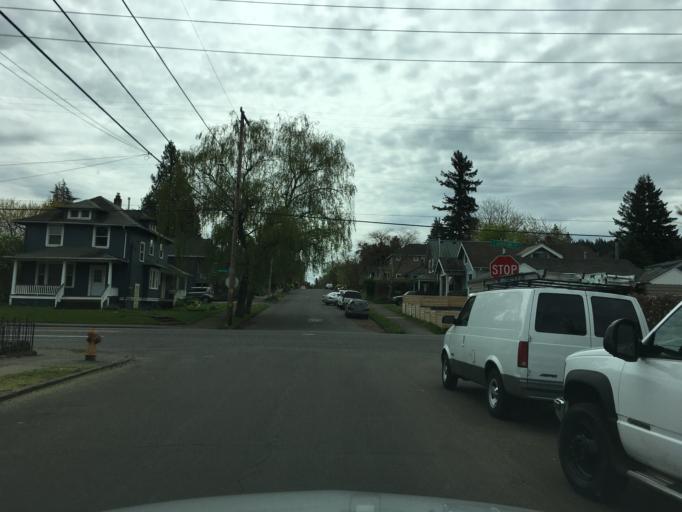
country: US
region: Oregon
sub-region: Multnomah County
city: Lents
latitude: 45.5231
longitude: -122.5859
